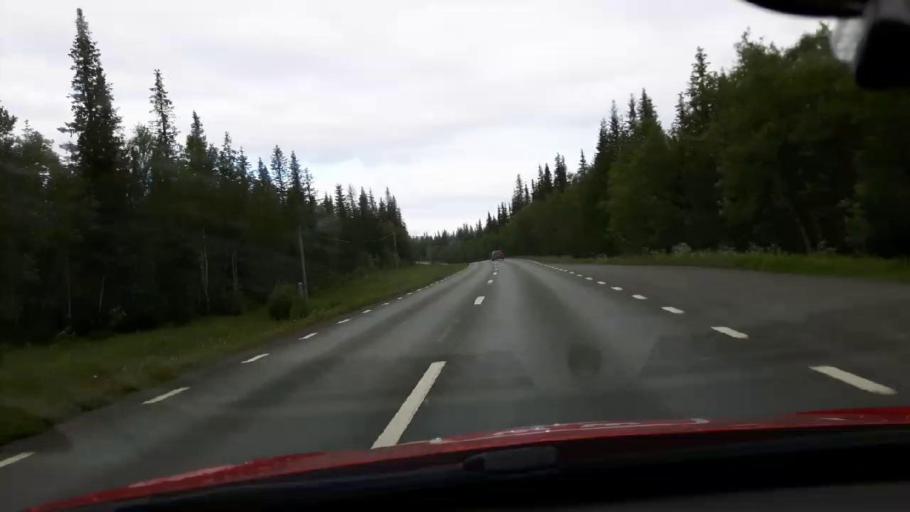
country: NO
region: Nord-Trondelag
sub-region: Meraker
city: Meraker
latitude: 63.2880
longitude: 12.3647
